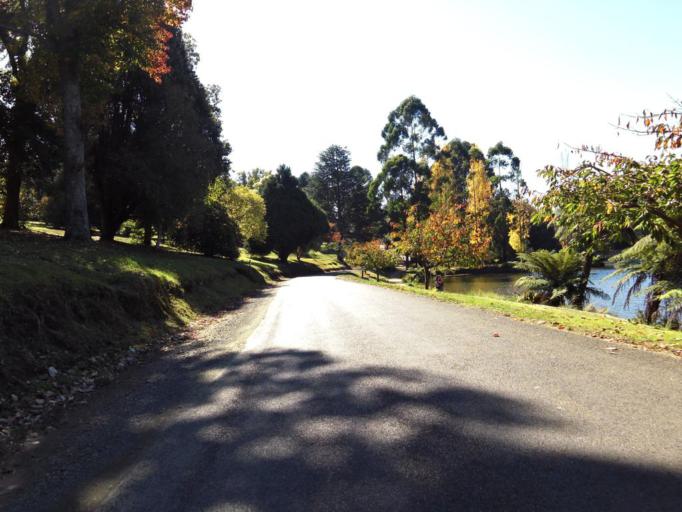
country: AU
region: Victoria
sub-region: Cardinia
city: Emerald
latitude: -37.9292
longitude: 145.4581
